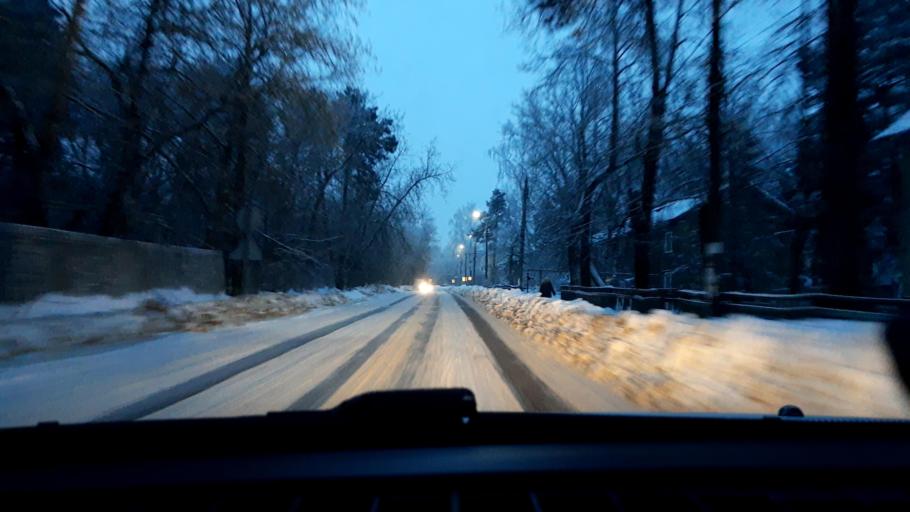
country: RU
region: Nizjnij Novgorod
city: Gidrotorf
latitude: 56.5245
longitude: 43.5481
